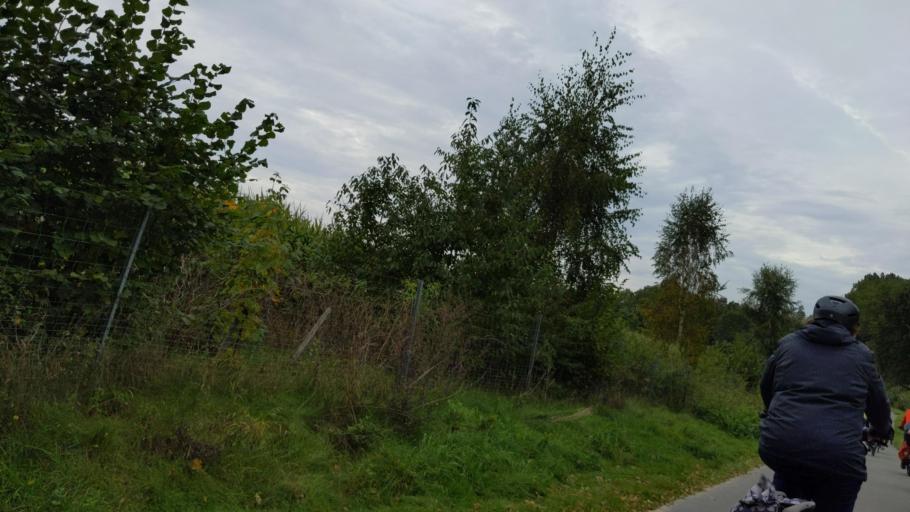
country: DE
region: Schleswig-Holstein
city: Gross Gronau
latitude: 53.7925
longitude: 10.7664
